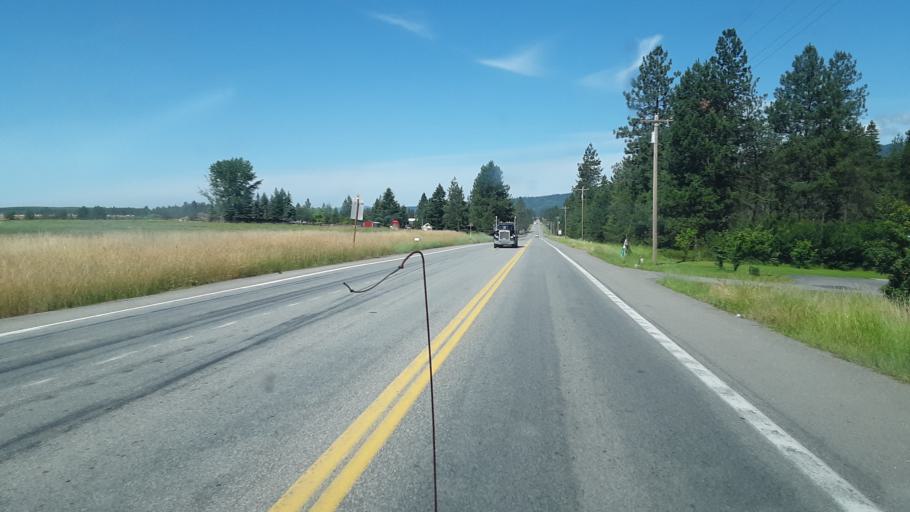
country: US
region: Idaho
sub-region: Kootenai County
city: Hayden
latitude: 47.8173
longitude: -116.8084
